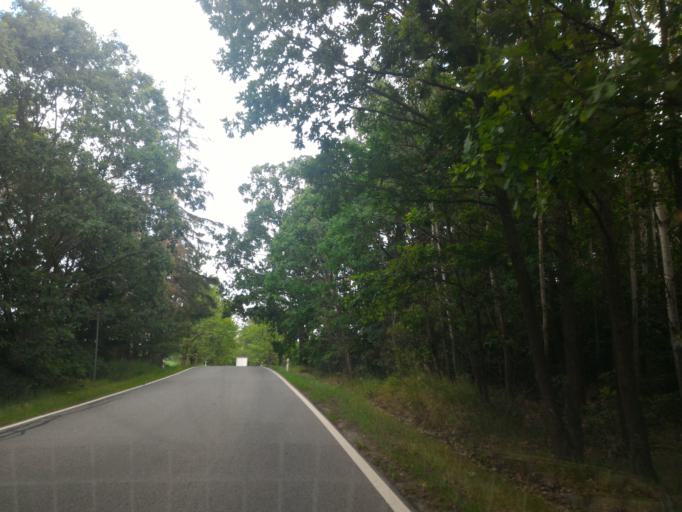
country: CZ
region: Vysocina
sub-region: Okres Jihlava
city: Telc
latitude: 49.2111
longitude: 15.4322
